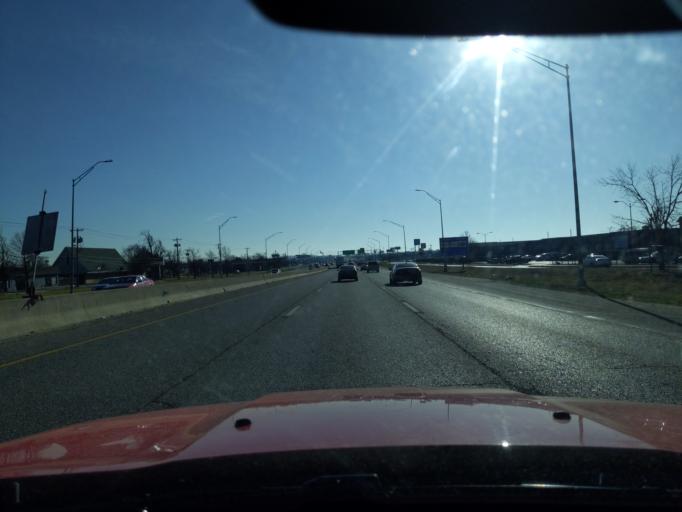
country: US
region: Oklahoma
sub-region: Cleveland County
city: Moore
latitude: 35.3915
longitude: -97.5386
